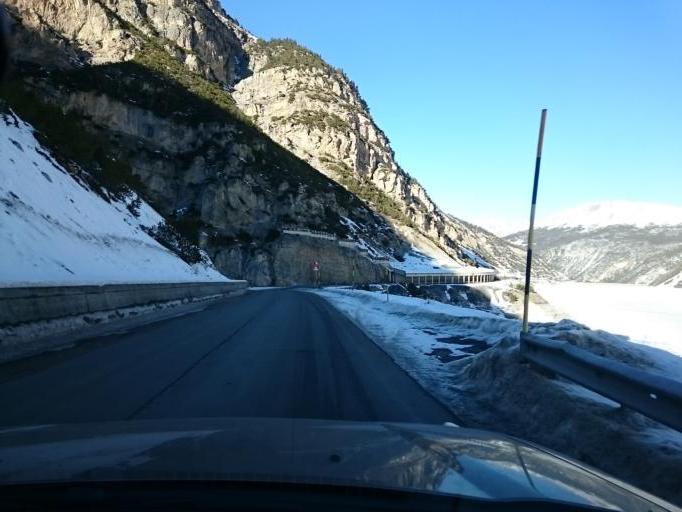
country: IT
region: Lombardy
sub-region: Provincia di Sondrio
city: Livigno
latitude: 46.6036
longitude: 10.1747
